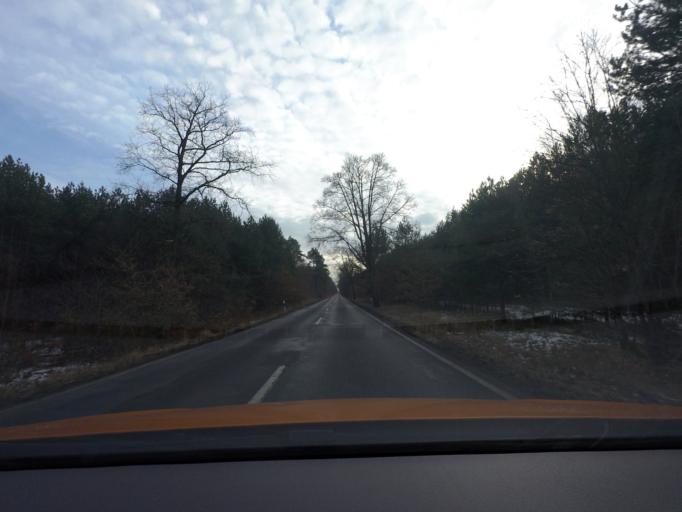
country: DE
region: Brandenburg
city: Wandlitz
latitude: 52.7269
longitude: 13.3679
